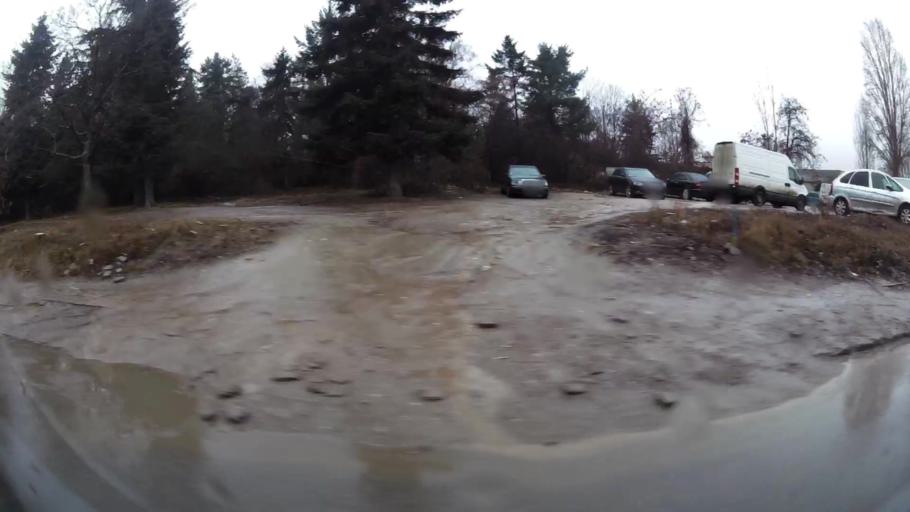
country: BG
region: Sofia-Capital
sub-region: Stolichna Obshtina
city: Sofia
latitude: 42.6383
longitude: 23.4064
